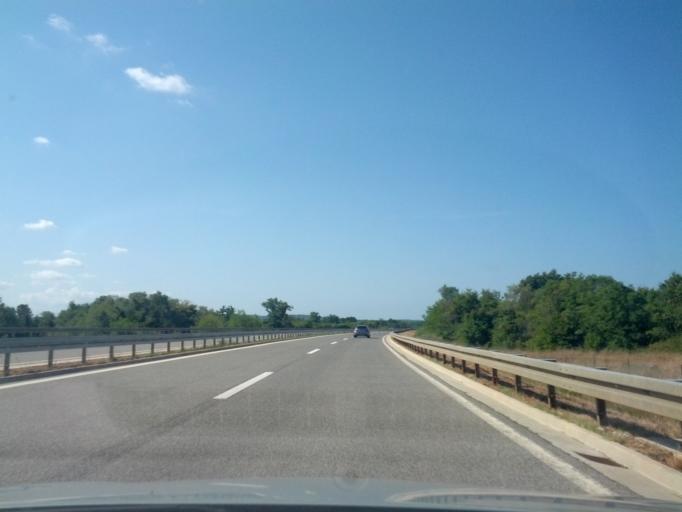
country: HR
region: Istarska
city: Vrsar
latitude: 45.1740
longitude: 13.7334
